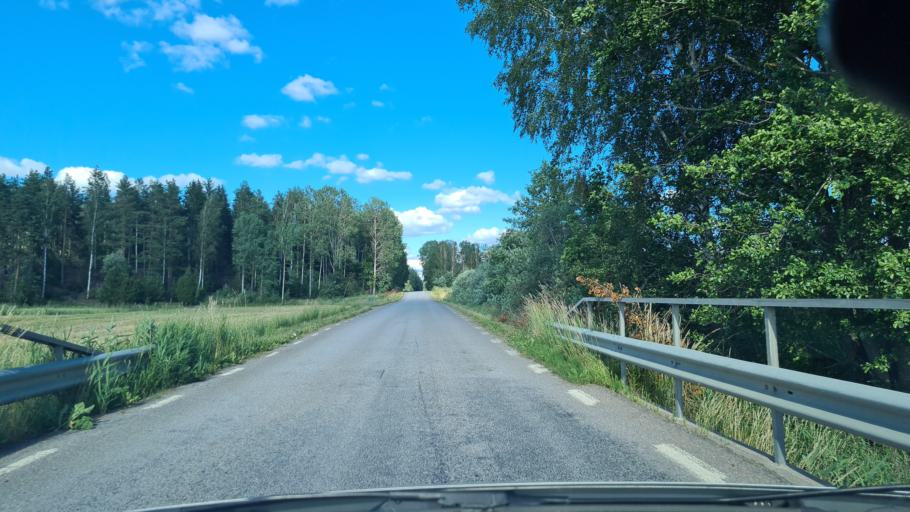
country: SE
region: Soedermanland
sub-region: Nykopings Kommun
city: Olstorp
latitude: 58.8182
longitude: 16.4868
